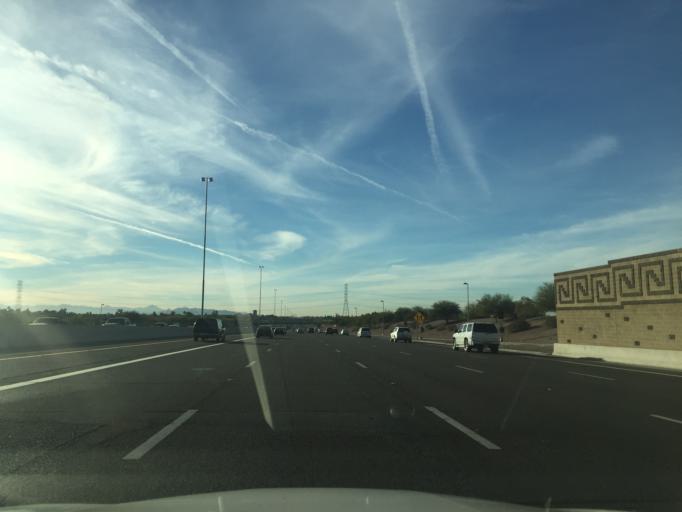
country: US
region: Arizona
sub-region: Maricopa County
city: Gilbert
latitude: 33.3866
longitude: -111.7398
